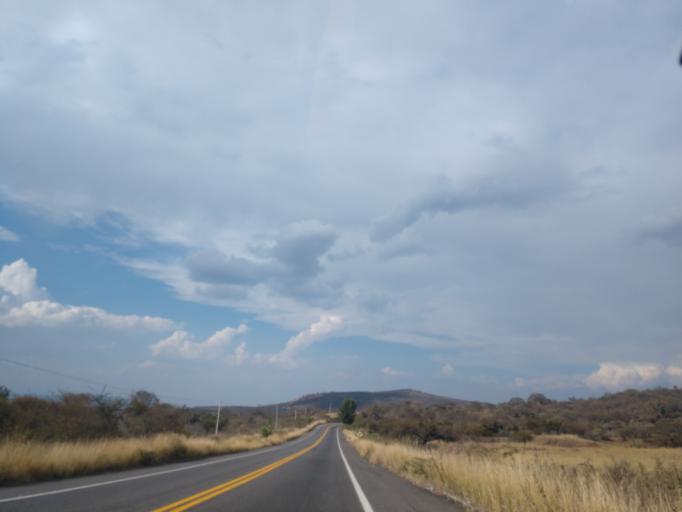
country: MX
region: Jalisco
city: La Manzanilla de la Paz
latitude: 20.0758
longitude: -103.1704
